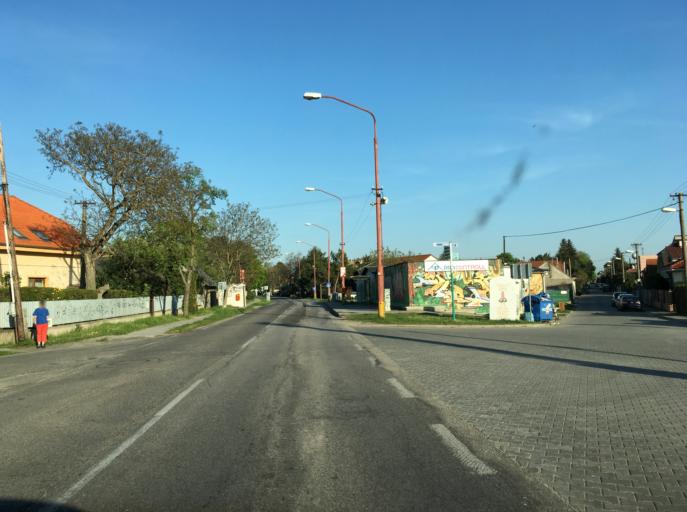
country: AT
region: Burgenland
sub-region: Politischer Bezirk Neusiedl am See
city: Deutsch Jahrndorf
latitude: 48.0581
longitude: 17.1379
